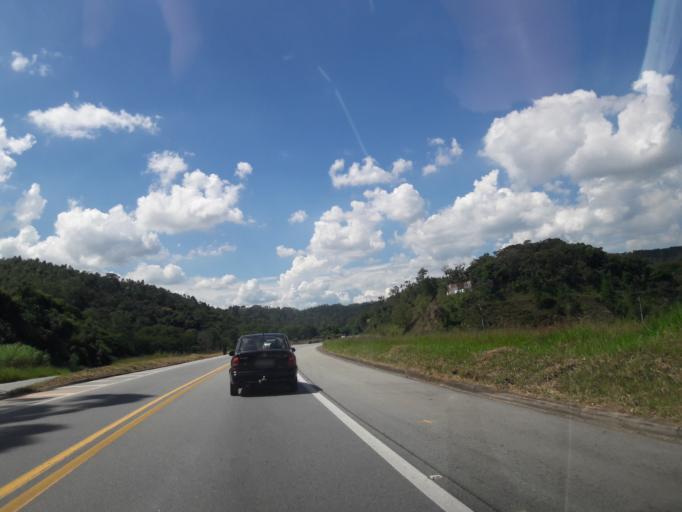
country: BR
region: Sao Paulo
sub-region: Francisco Morato
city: Francisco Morato
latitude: -23.2866
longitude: -46.7999
